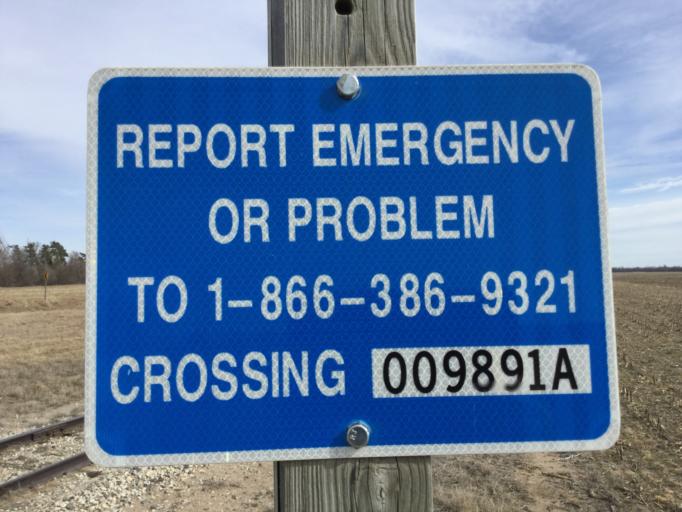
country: US
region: Kansas
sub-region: Rice County
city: Sterling
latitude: 38.2529
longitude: -98.3442
